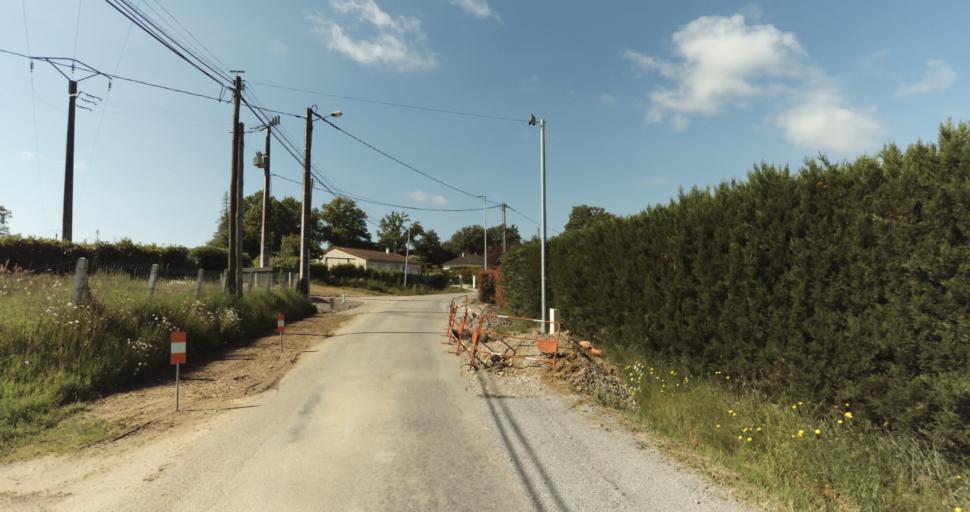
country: FR
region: Limousin
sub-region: Departement de la Haute-Vienne
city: Le Vigen
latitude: 45.7350
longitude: 1.2867
